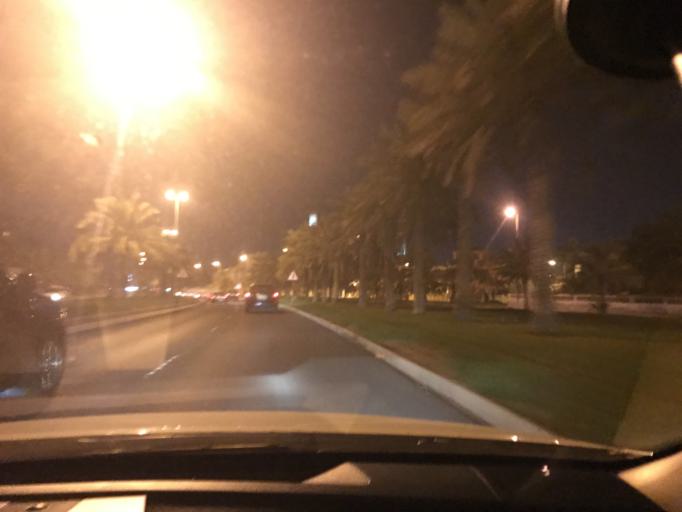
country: BH
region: Muharraq
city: Al Muharraq
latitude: 26.2559
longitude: 50.6221
